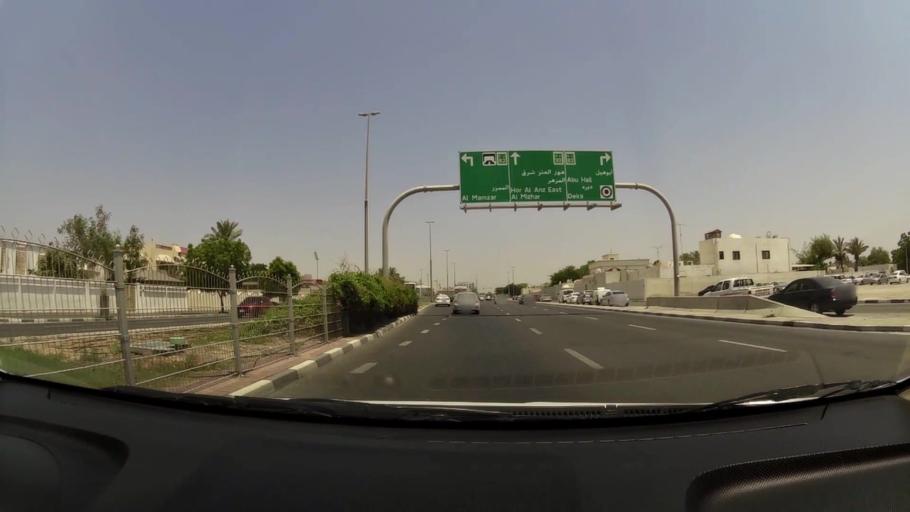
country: AE
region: Ash Shariqah
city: Sharjah
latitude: 25.2917
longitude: 55.3437
